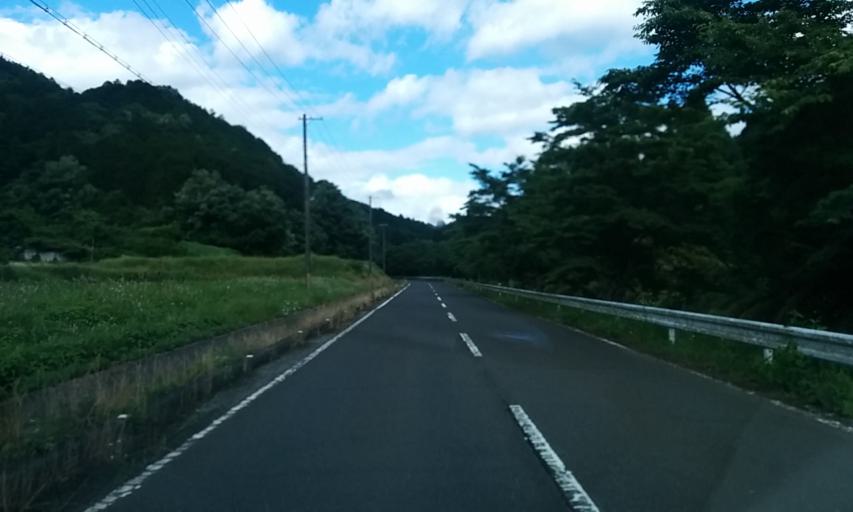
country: JP
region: Kyoto
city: Ayabe
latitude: 35.3618
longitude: 135.2258
